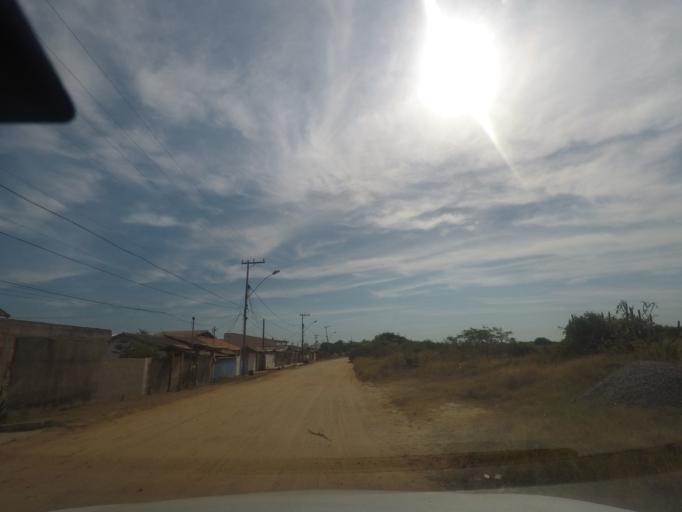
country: BR
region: Rio de Janeiro
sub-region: Marica
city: Marica
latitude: -22.9597
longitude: -42.8365
